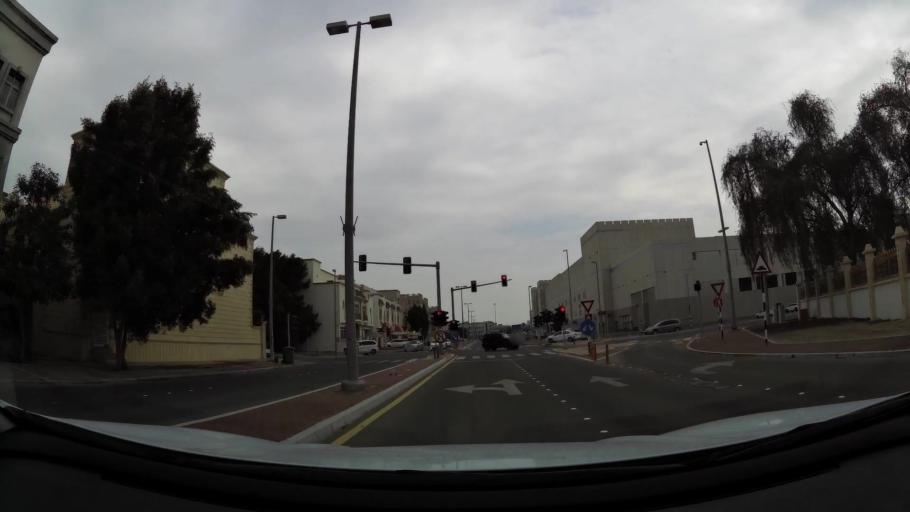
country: AE
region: Abu Dhabi
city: Abu Dhabi
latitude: 24.4364
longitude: 54.4114
